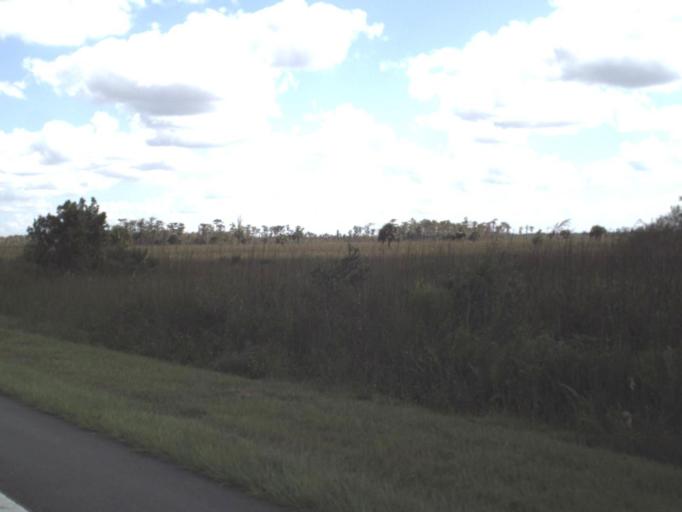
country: US
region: Florida
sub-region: Collier County
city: Marco
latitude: 25.8757
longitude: -81.2184
